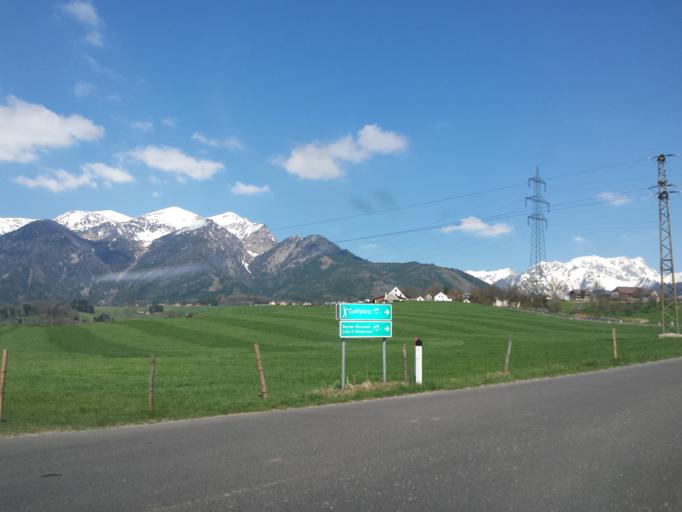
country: AT
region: Styria
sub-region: Politischer Bezirk Leoben
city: Trofaiach
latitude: 47.4082
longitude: 14.9738
